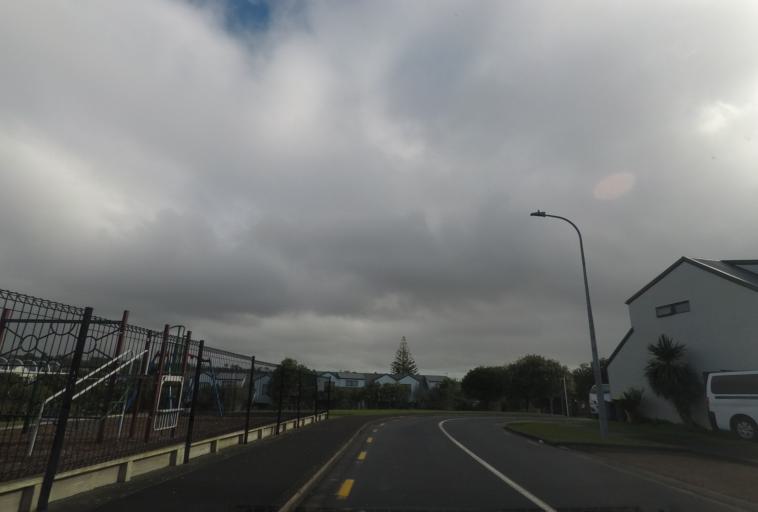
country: NZ
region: Auckland
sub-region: Auckland
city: Waitakere
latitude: -36.9033
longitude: 174.6623
